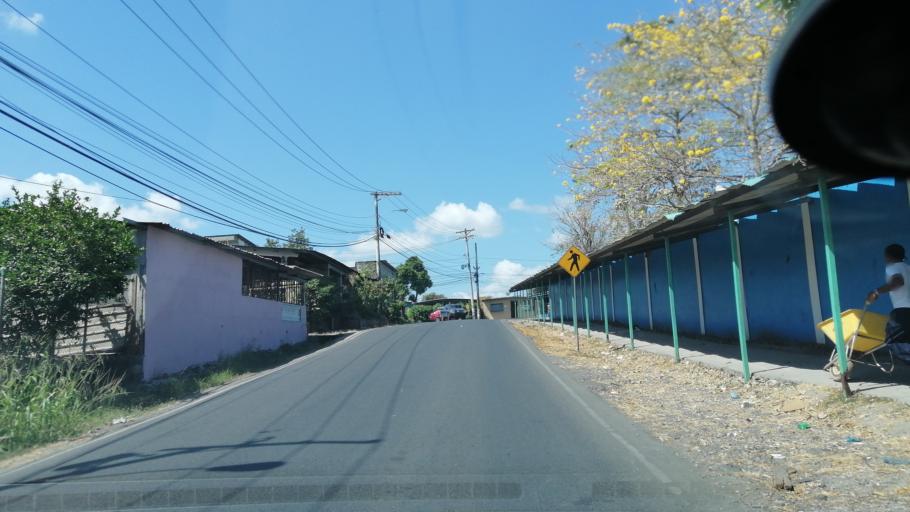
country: PA
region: Panama
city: Las Cumbres
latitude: 9.0801
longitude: -79.4949
